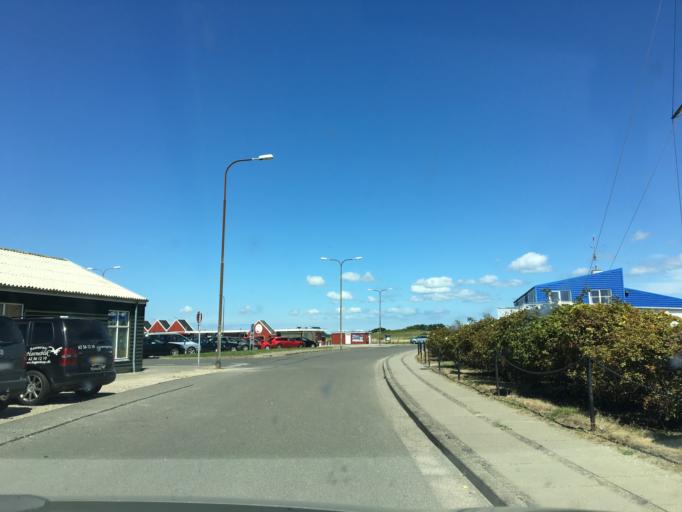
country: DK
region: South Denmark
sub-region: Langeland Kommune
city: Rudkobing
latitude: 54.7509
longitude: 10.6749
